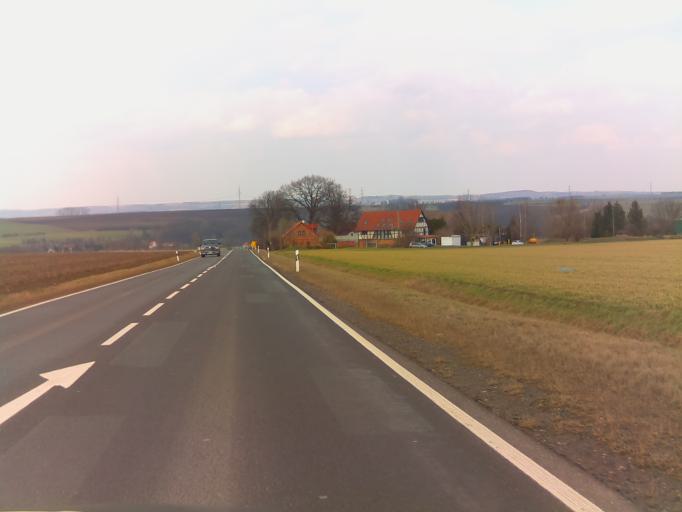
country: DE
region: Thuringia
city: Mattstedt
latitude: 51.0467
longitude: 11.5146
